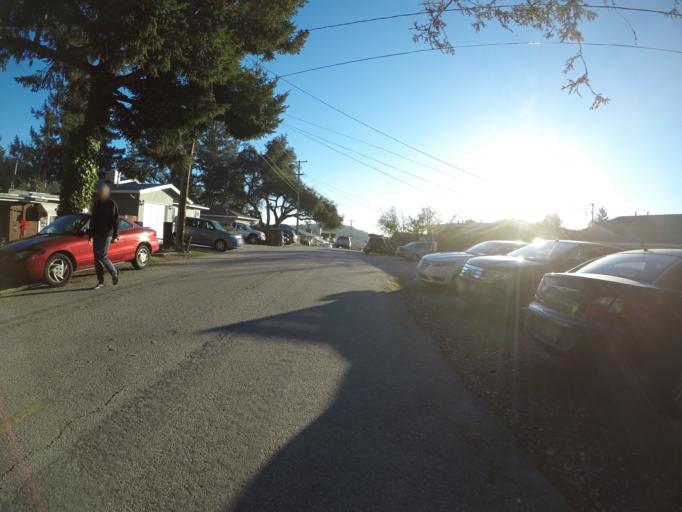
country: US
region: California
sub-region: Santa Cruz County
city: Scotts Valley
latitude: 37.0709
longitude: -121.9964
